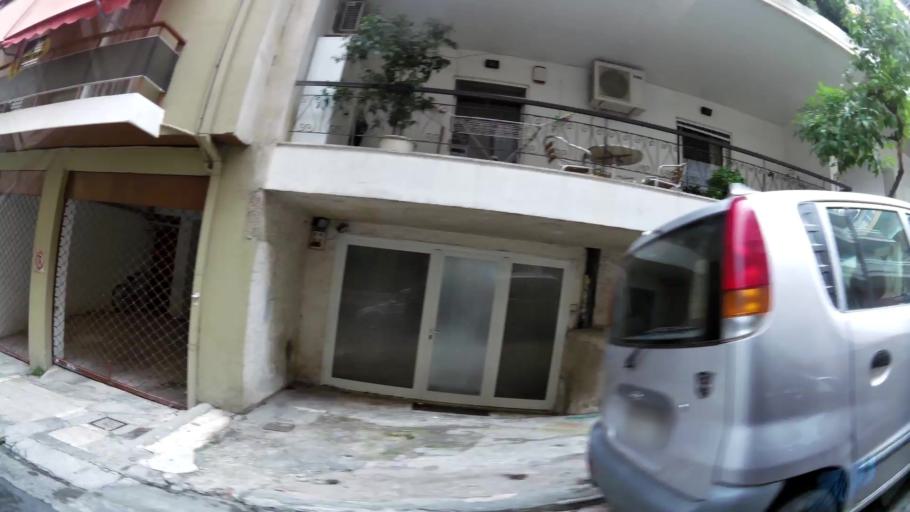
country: GR
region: Attica
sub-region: Nomos Attikis
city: Piraeus
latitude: 37.9459
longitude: 23.6554
